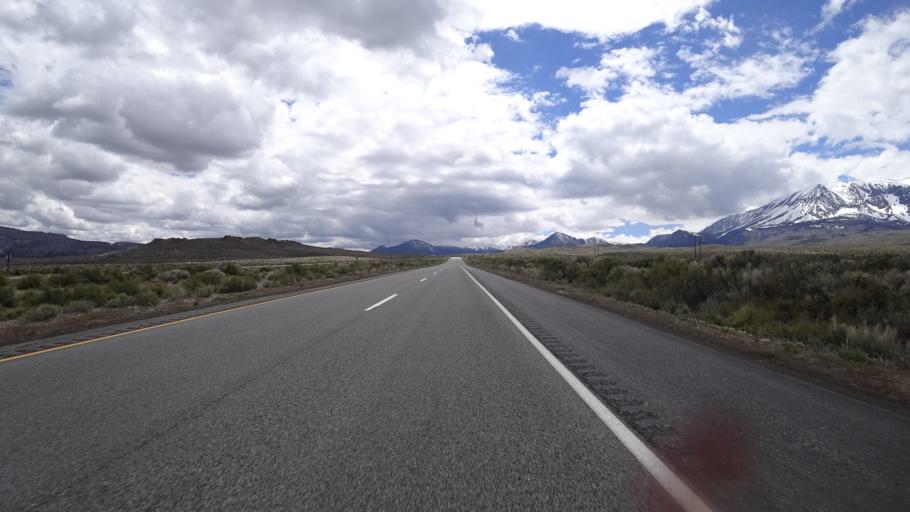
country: US
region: California
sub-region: Mono County
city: Mammoth Lakes
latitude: 37.8730
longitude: -119.0887
